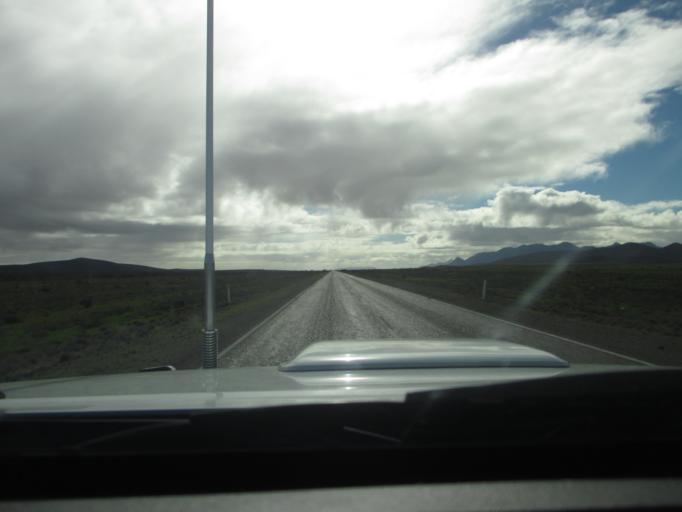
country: AU
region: South Australia
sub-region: Flinders Ranges
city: Quorn
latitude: -31.6564
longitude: 138.3771
